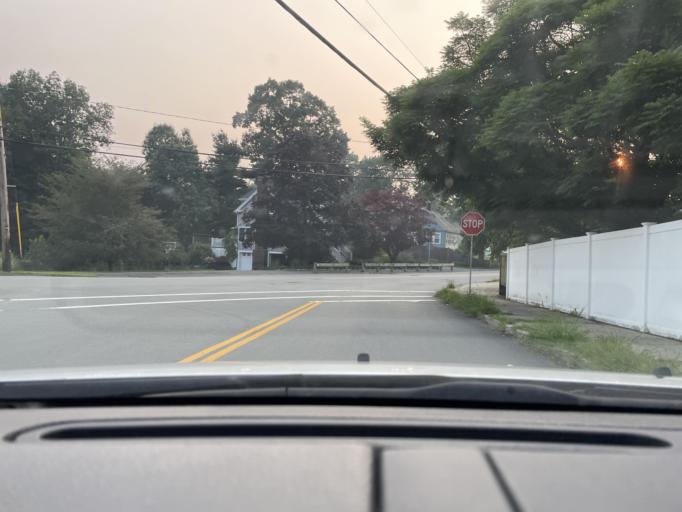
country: US
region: Massachusetts
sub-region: Middlesex County
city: Stoneham
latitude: 42.4868
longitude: -71.1025
